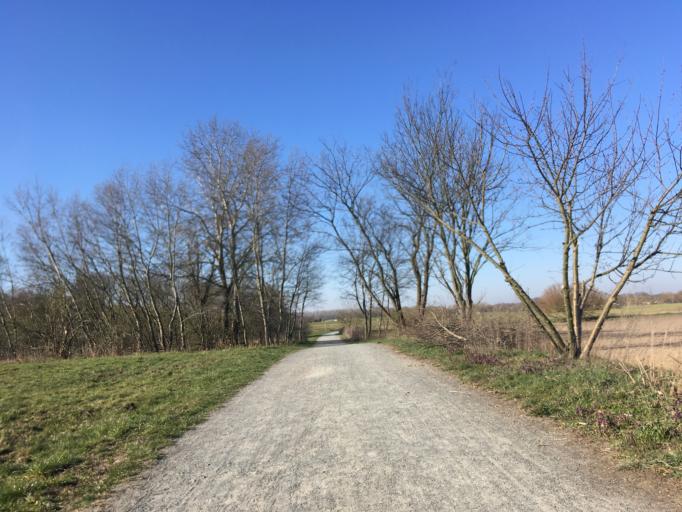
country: DE
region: Berlin
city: Blankenfelde
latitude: 52.6243
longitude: 13.4155
